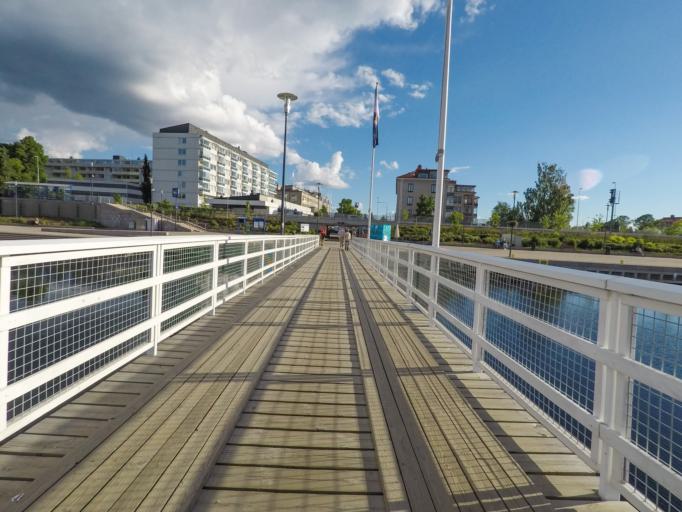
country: FI
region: Southern Savonia
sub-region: Savonlinna
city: Savonlinna
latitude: 61.8696
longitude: 28.8873
